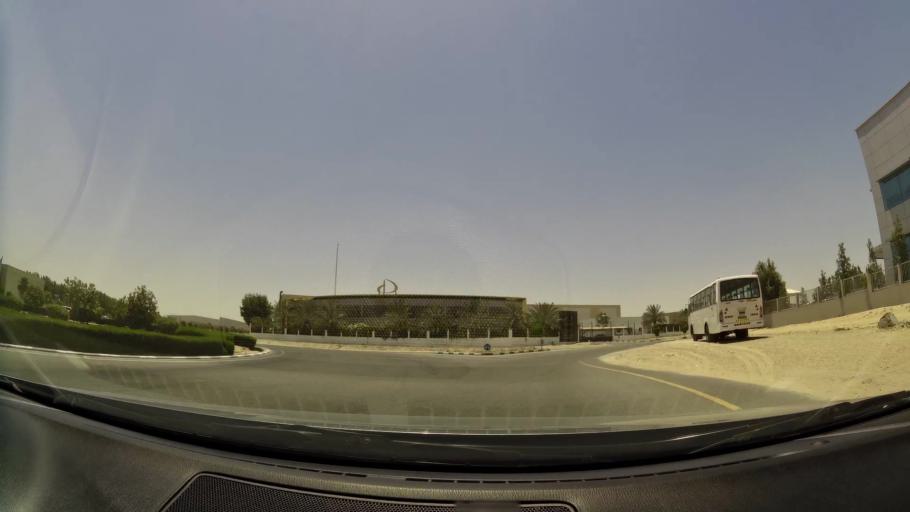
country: AE
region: Dubai
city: Dubai
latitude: 24.9846
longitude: 55.2066
